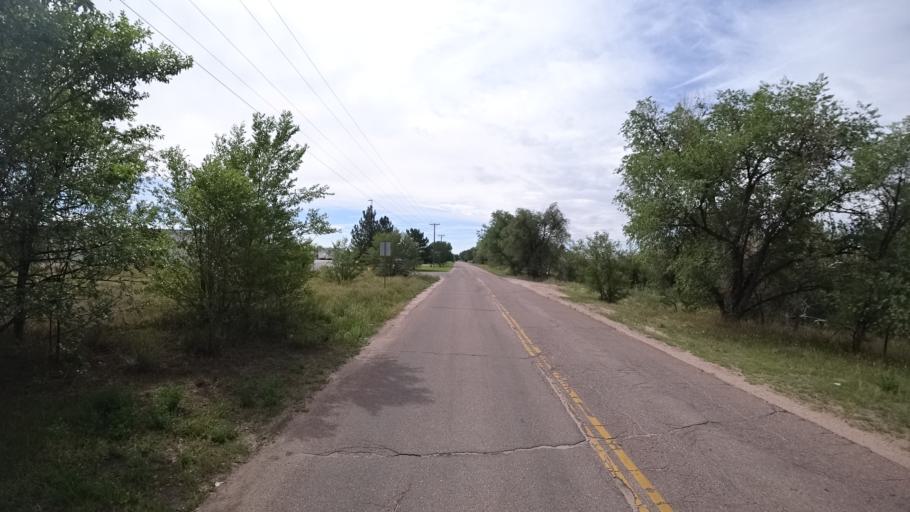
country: US
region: Colorado
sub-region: El Paso County
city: Security-Widefield
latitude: 38.7409
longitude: -104.7387
